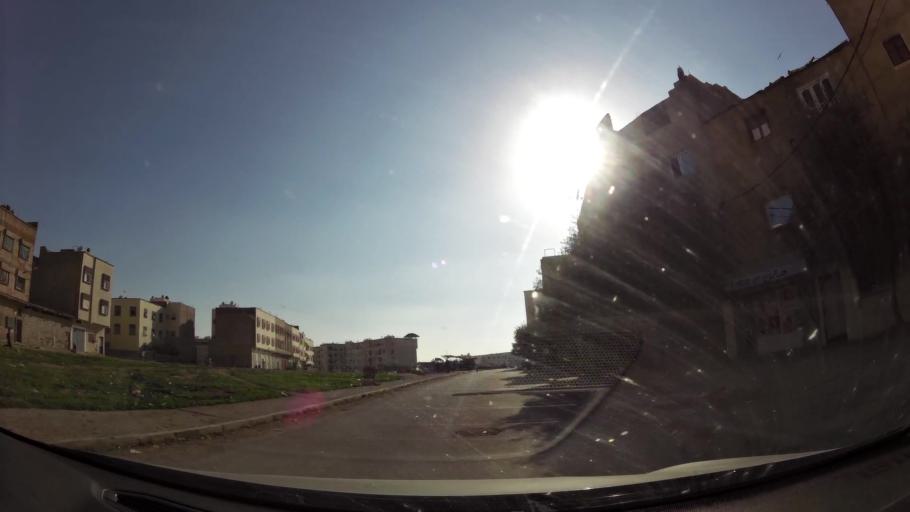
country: MA
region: Fes-Boulemane
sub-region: Fes
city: Fes
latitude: 34.0177
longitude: -5.0394
